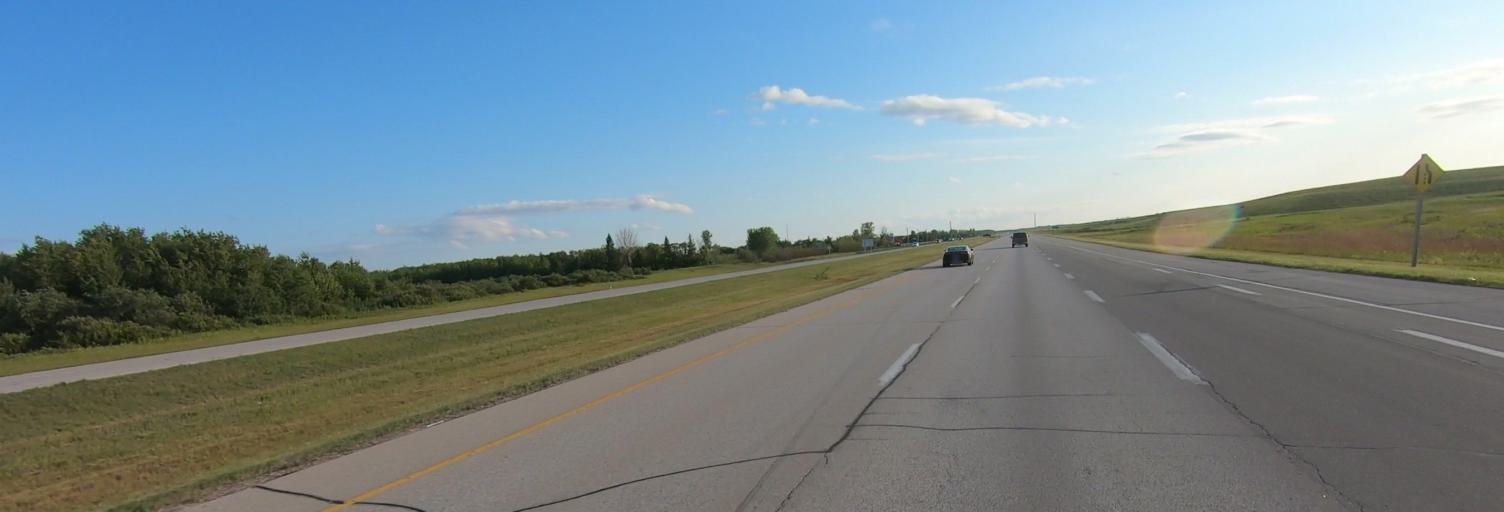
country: CA
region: Manitoba
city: Selkirk
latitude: 50.0139
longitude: -96.9495
